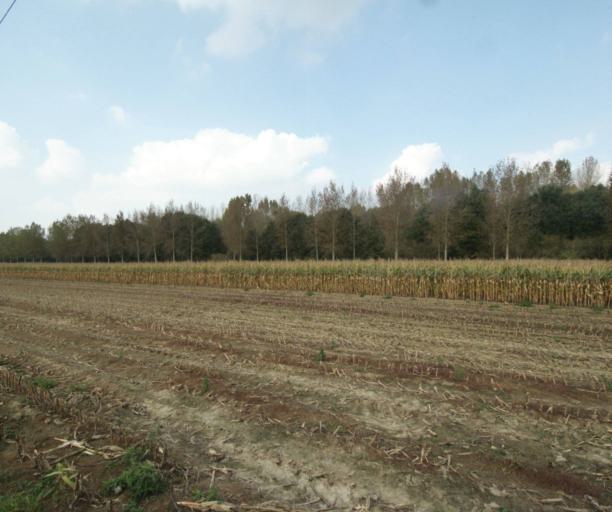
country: FR
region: Nord-Pas-de-Calais
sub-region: Departement du Nord
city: Emmerin
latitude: 50.5809
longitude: 2.9940
